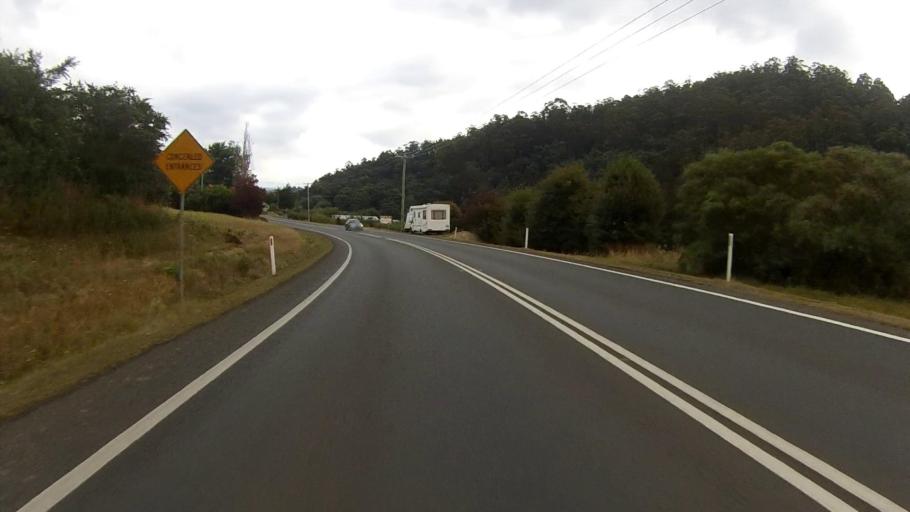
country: AU
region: Tasmania
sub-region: Huon Valley
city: Cygnet
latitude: -43.1414
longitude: 147.0636
